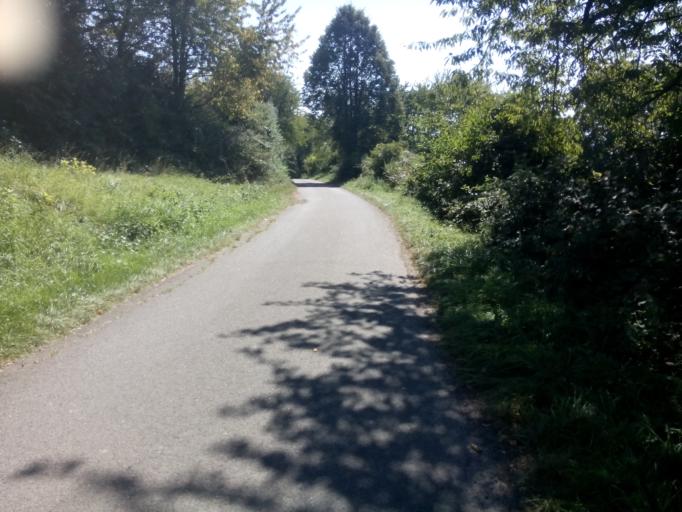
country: DE
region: Hesse
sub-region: Regierungsbezirk Darmstadt
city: Brensbach
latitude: 49.8194
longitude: 8.9082
